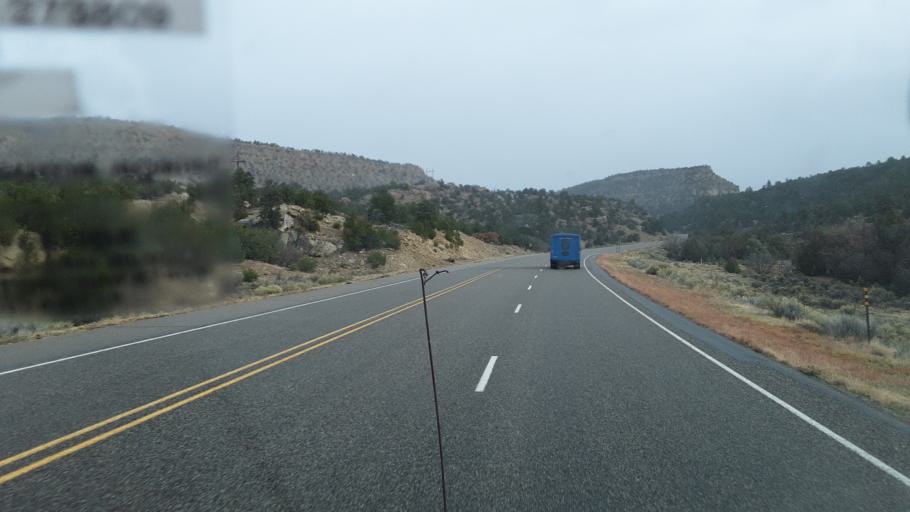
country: US
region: New Mexico
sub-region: Rio Arriba County
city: Tierra Amarilla
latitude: 36.4044
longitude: -106.4926
